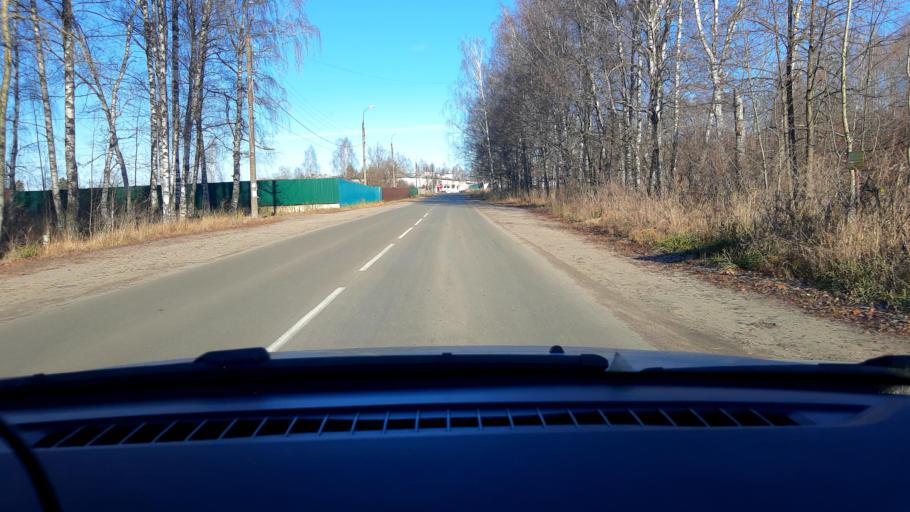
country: RU
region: Nizjnij Novgorod
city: Novosmolinskiy
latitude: 56.2793
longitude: 43.0224
